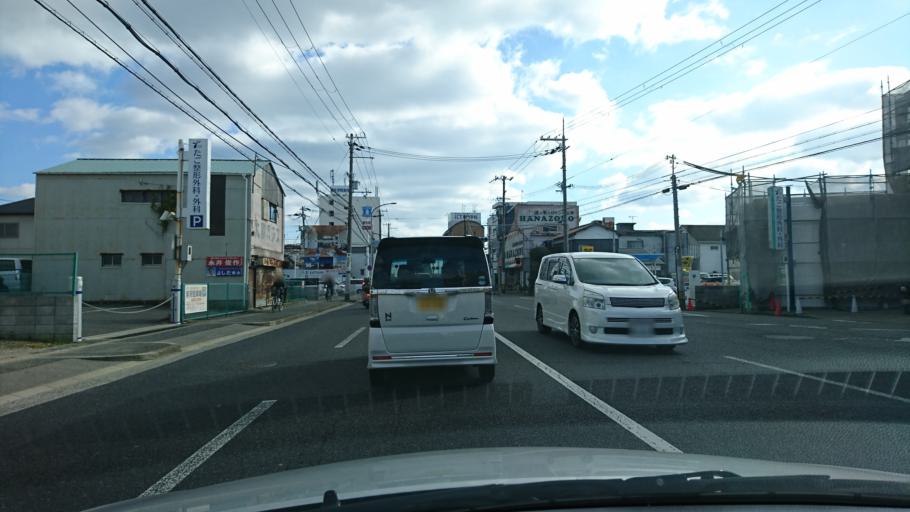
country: JP
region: Hyogo
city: Akashi
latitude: 34.6640
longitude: 134.9649
